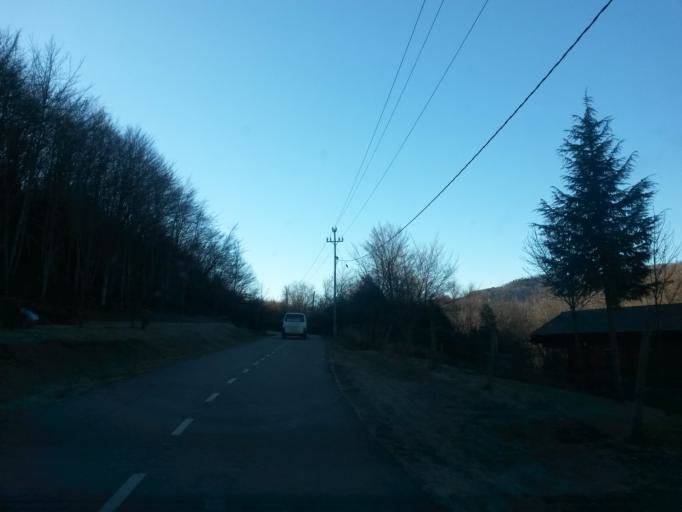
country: ES
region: Catalonia
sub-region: Provincia de Girona
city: Sant Feliu de Pallerols
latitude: 42.0464
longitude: 2.5111
